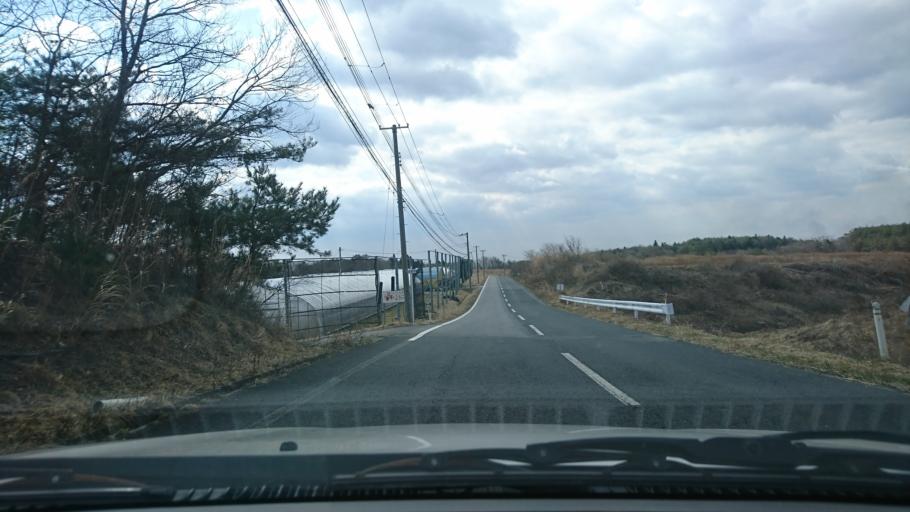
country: JP
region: Iwate
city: Ichinoseki
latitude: 38.8067
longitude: 141.2623
